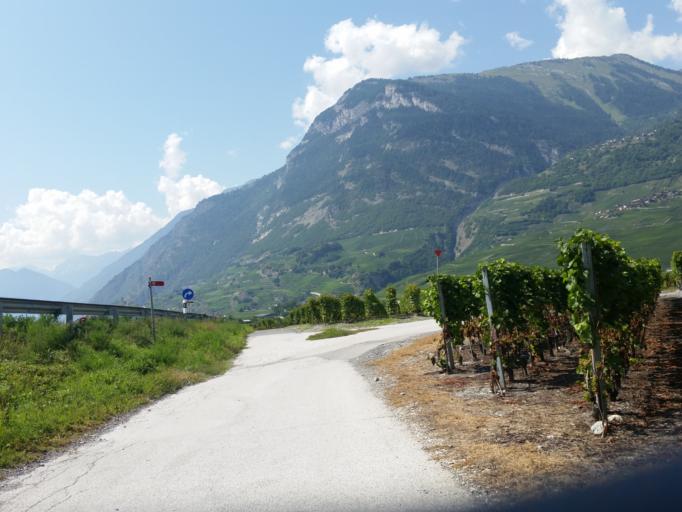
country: CH
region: Valais
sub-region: Martigny District
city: Riddes
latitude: 46.1821
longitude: 7.2192
